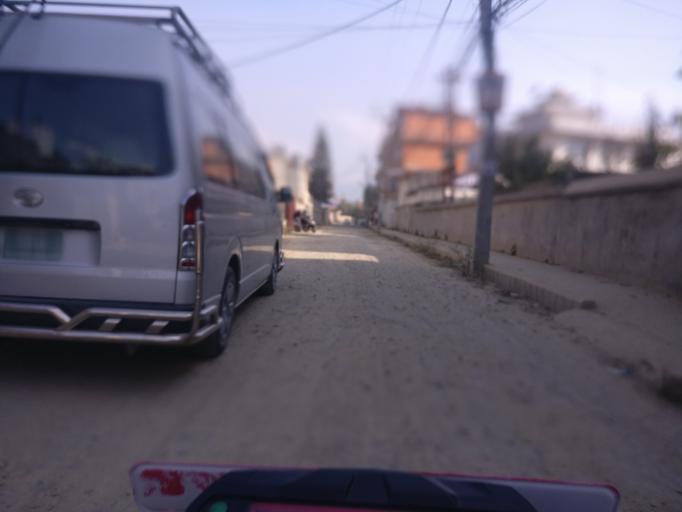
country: NP
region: Central Region
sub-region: Bagmati Zone
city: Patan
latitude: 27.6811
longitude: 85.3206
